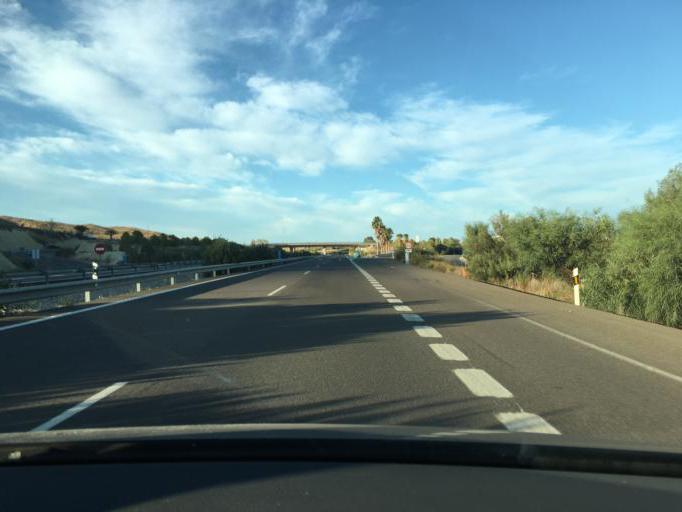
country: ES
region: Andalusia
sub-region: Provincia de Almeria
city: Bedar
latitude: 37.1549
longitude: -1.9530
